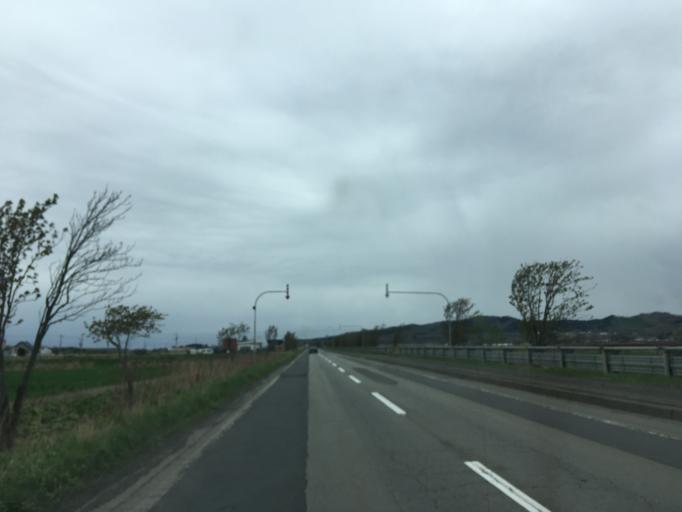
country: JP
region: Hokkaido
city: Chitose
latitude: 42.9495
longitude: 141.7945
